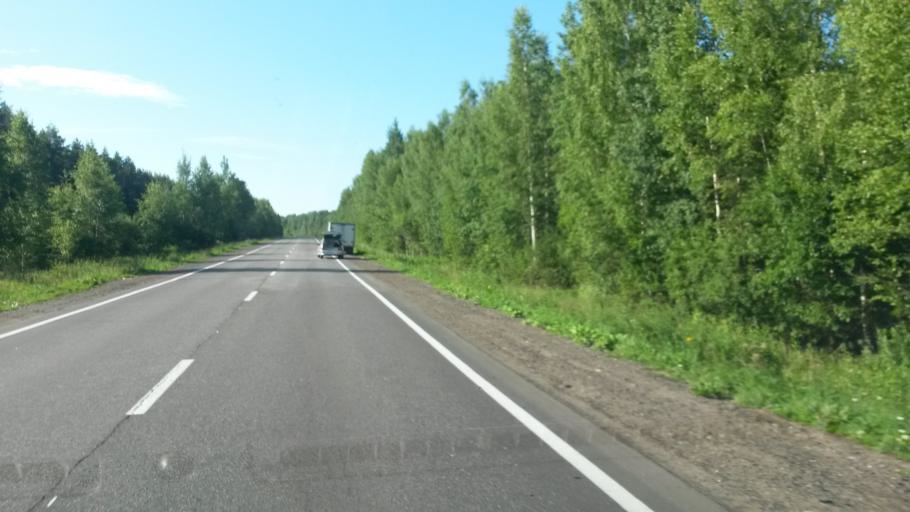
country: RU
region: Jaroslavl
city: Gavrilov-Yam
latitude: 57.2969
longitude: 39.9491
